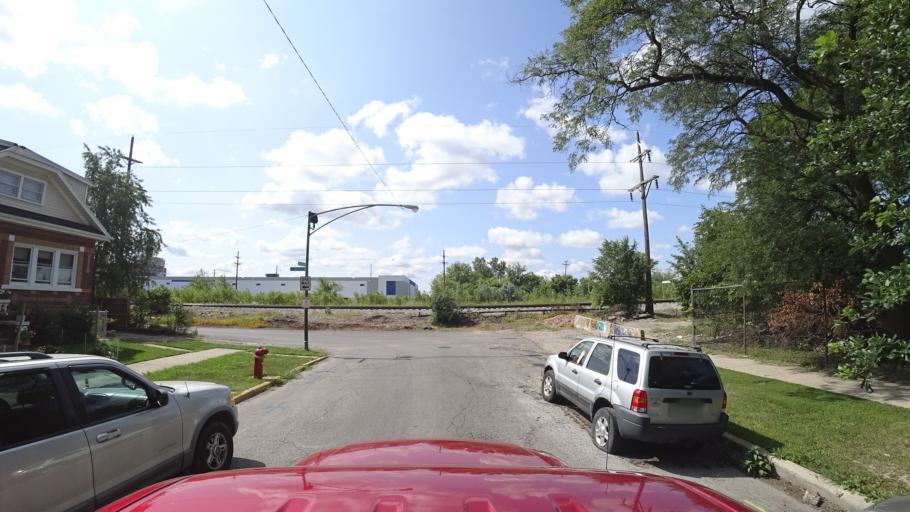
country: US
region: Illinois
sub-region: Cook County
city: Cicero
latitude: 41.8334
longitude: -87.7292
